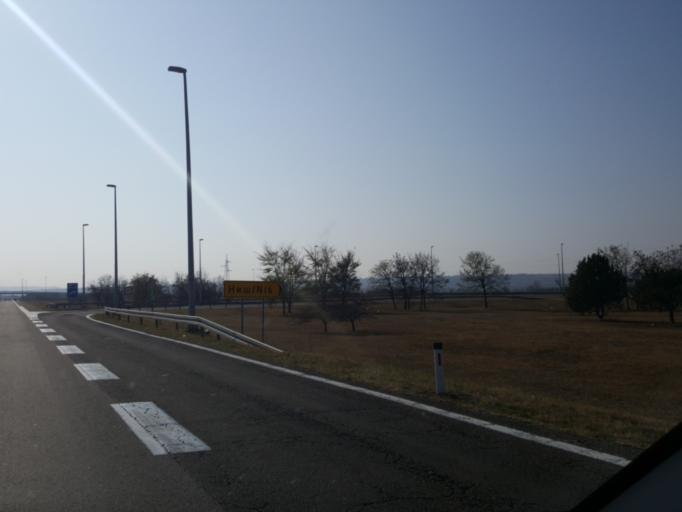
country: RS
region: Central Serbia
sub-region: Nisavski Okrug
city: Nis
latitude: 43.3278
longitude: 21.8107
